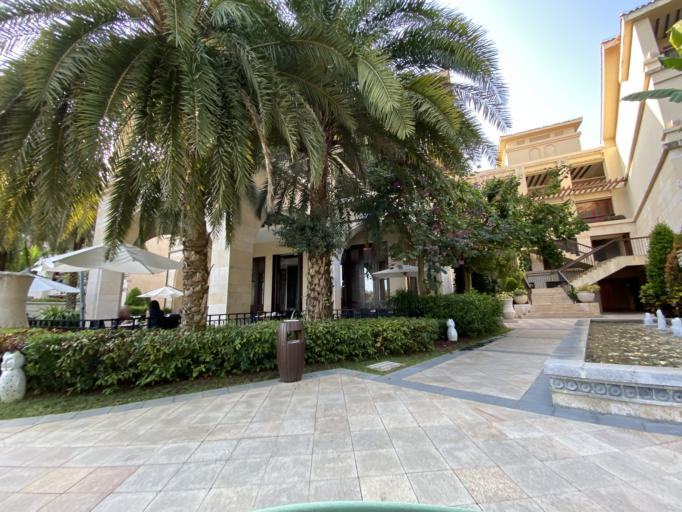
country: CN
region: Hainan
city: Haitangwan
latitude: 18.3498
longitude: 109.7379
